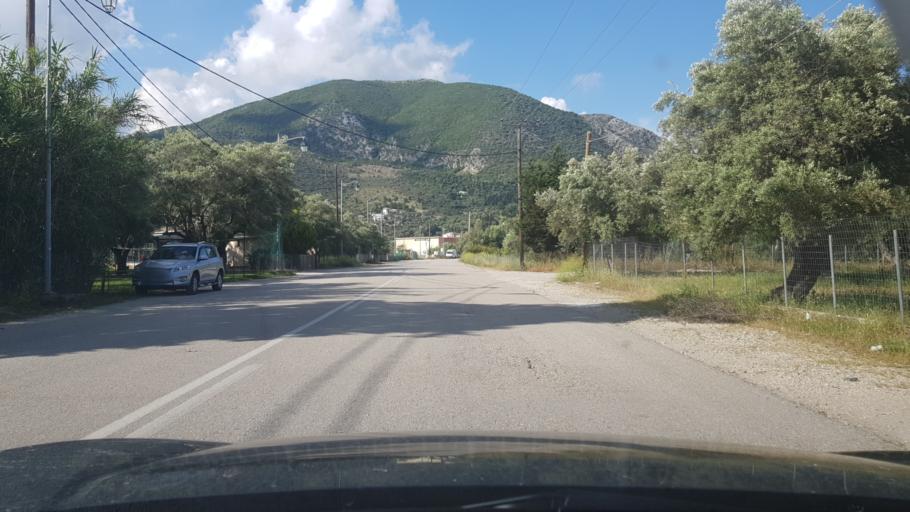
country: GR
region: Ionian Islands
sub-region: Lefkada
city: Nidri
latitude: 38.7070
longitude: 20.7041
